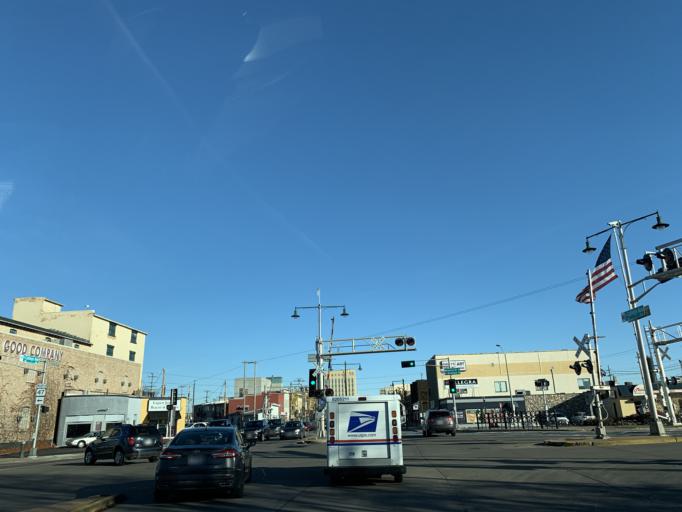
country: US
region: Wisconsin
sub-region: Outagamie County
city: Appleton
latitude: 44.2618
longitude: -88.4160
